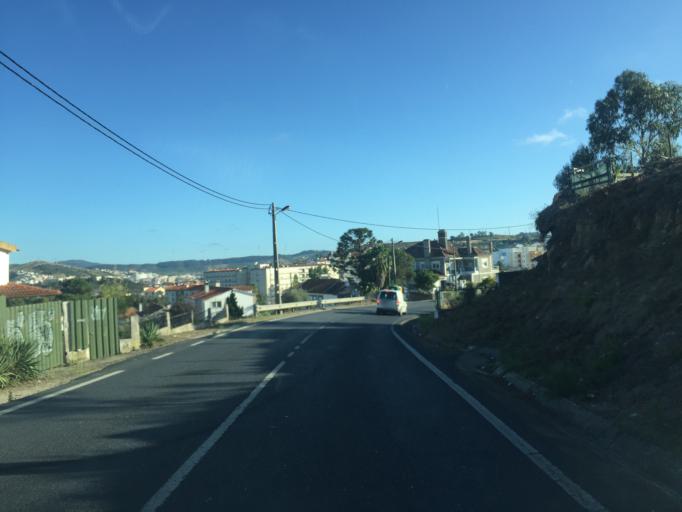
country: PT
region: Lisbon
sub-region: Torres Vedras
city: Torres Vedras
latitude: 39.1103
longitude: -9.2619
